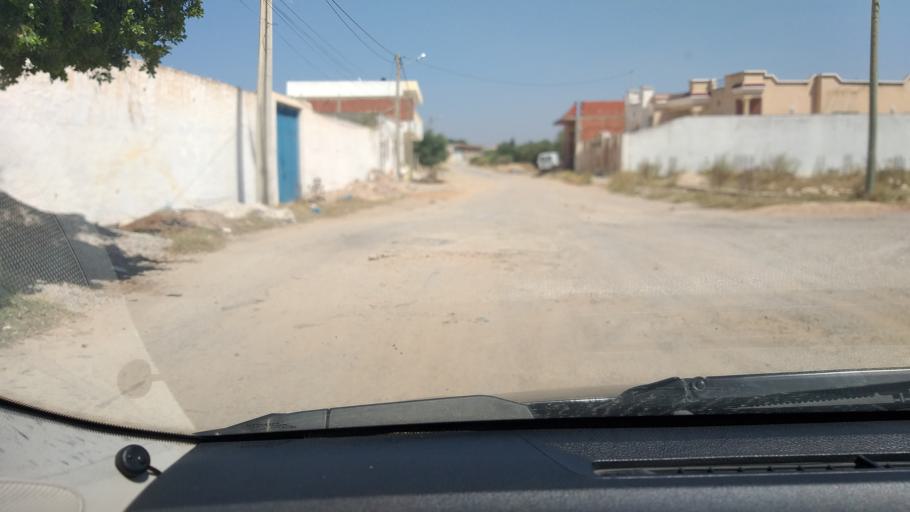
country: TN
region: Al Mahdiyah
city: El Jem
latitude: 35.2896
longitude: 10.7196
